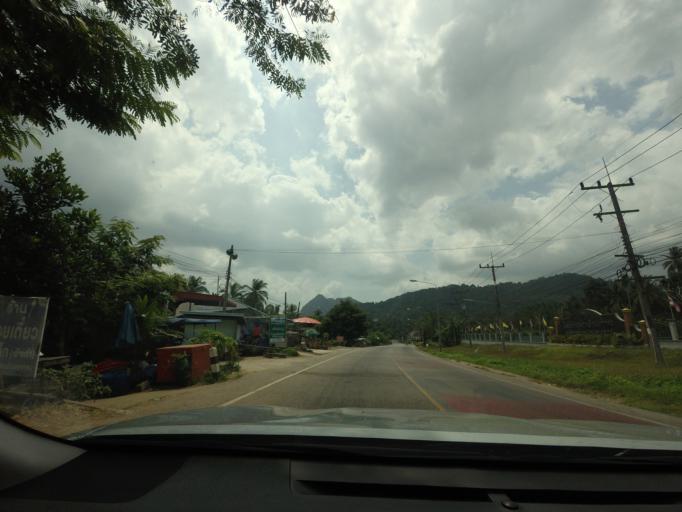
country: TH
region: Phangnga
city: Ban Ao Nang
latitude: 8.1068
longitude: 98.8025
